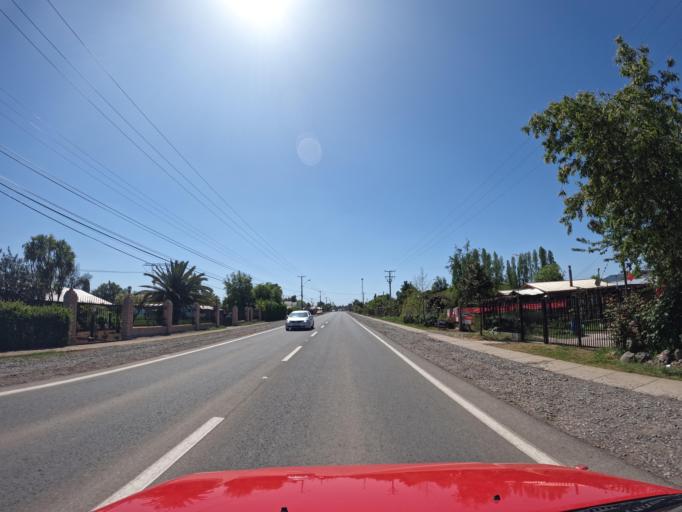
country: CL
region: Maule
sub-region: Provincia de Linares
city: Colbun
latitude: -35.7380
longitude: -71.4217
